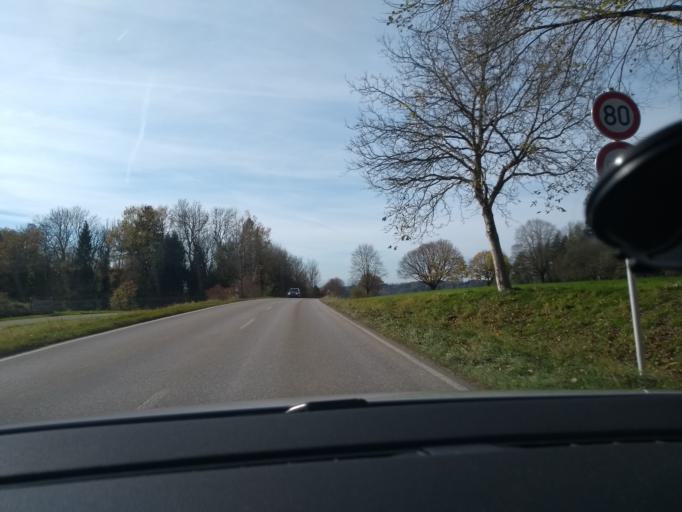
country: DE
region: Bavaria
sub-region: Upper Bavaria
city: Bad Endorf
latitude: 47.9055
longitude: 12.2874
